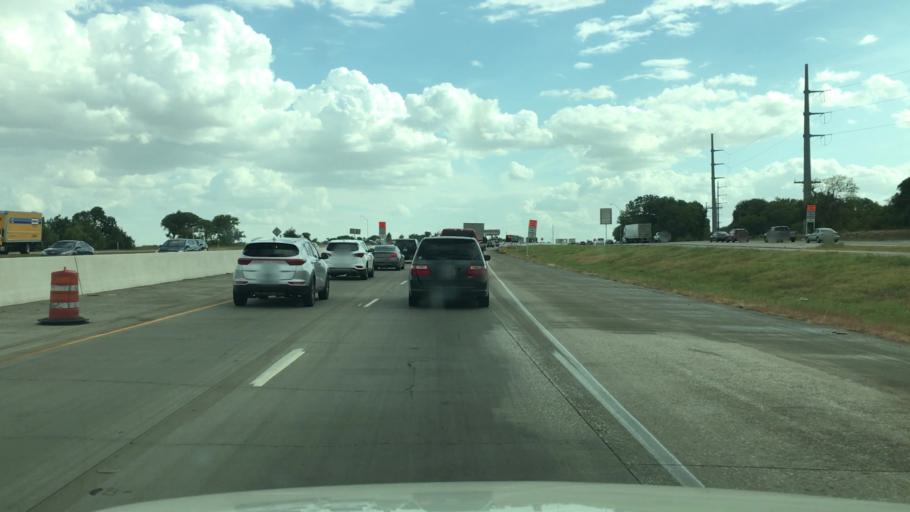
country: US
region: Texas
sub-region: McLennan County
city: Bruceville-Eddy
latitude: 31.3297
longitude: -97.2269
